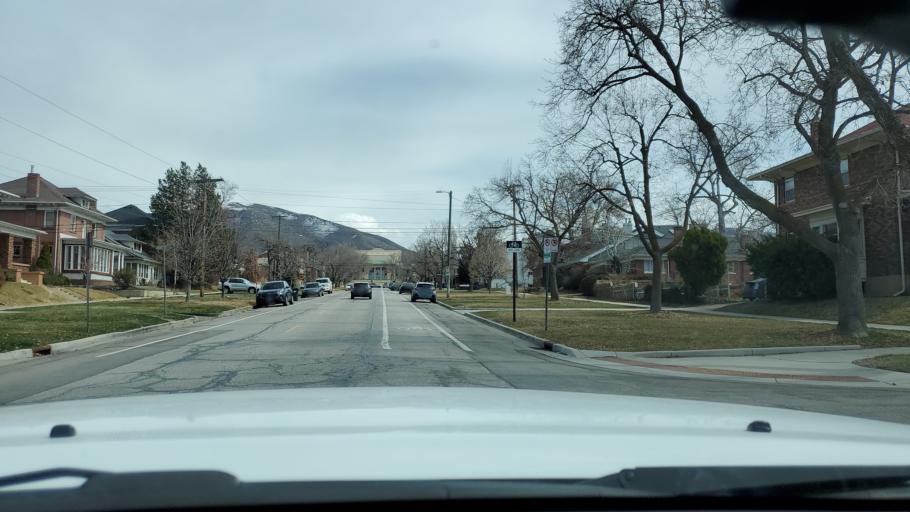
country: US
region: Utah
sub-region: Salt Lake County
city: Salt Lake City
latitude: 40.7628
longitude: -111.8567
